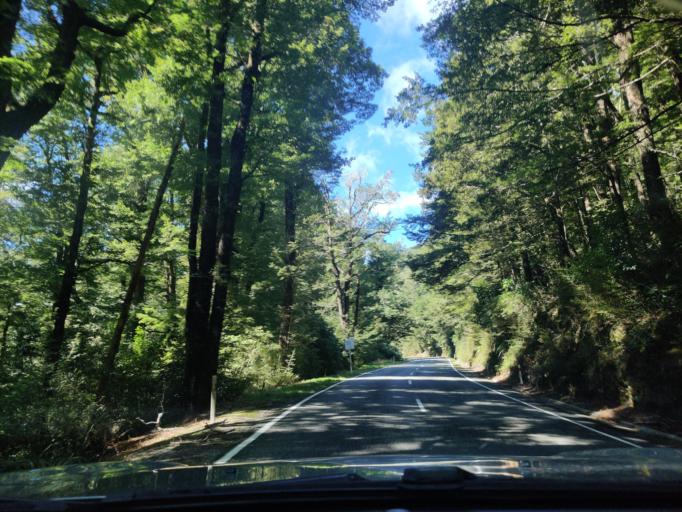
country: NZ
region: Canterbury
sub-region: Hurunui District
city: Amberley
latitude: -42.3794
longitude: 172.3419
